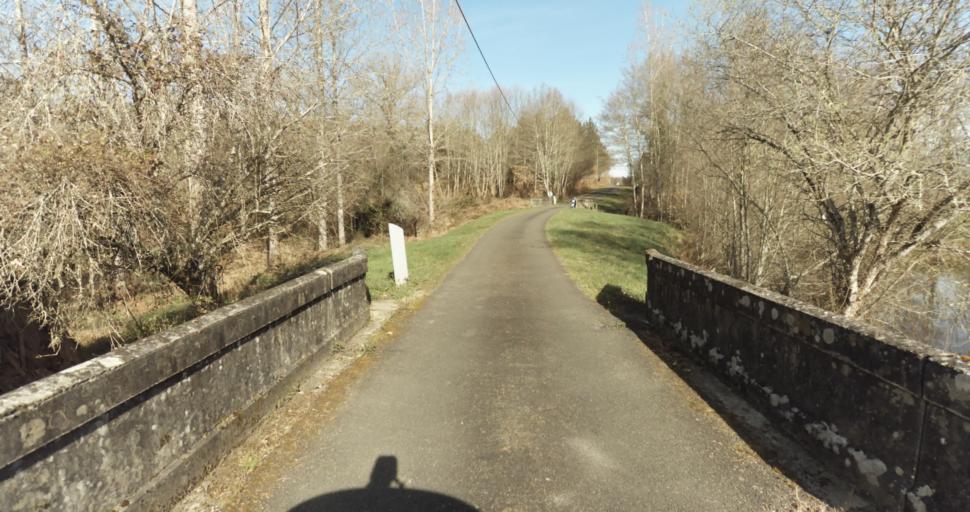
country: FR
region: Aquitaine
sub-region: Departement des Landes
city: Roquefort
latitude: 44.1190
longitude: -0.3024
